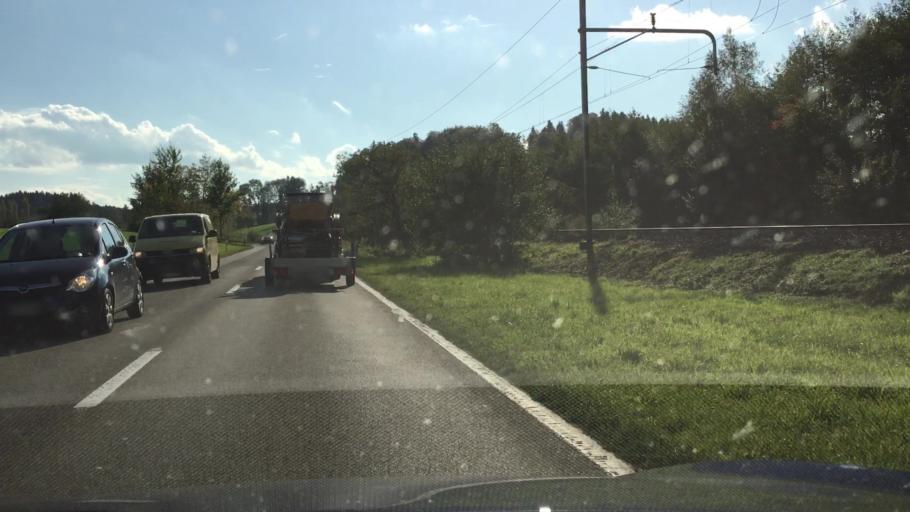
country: CH
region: Saint Gallen
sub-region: Wahlkreis St. Gallen
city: Waldkirch
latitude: 47.4643
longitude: 9.2489
